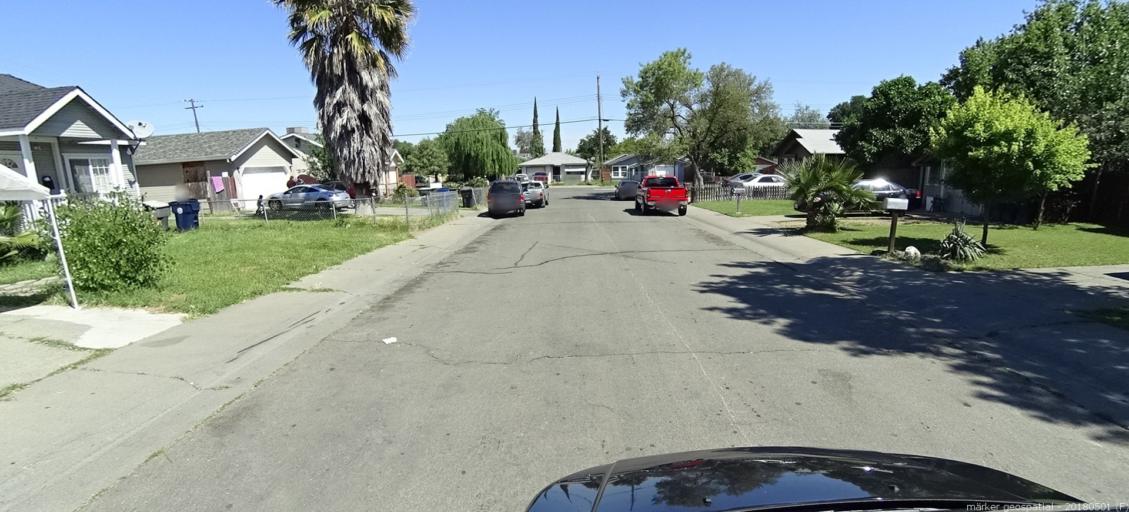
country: US
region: California
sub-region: Sacramento County
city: Rio Linda
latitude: 38.6396
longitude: -121.4396
